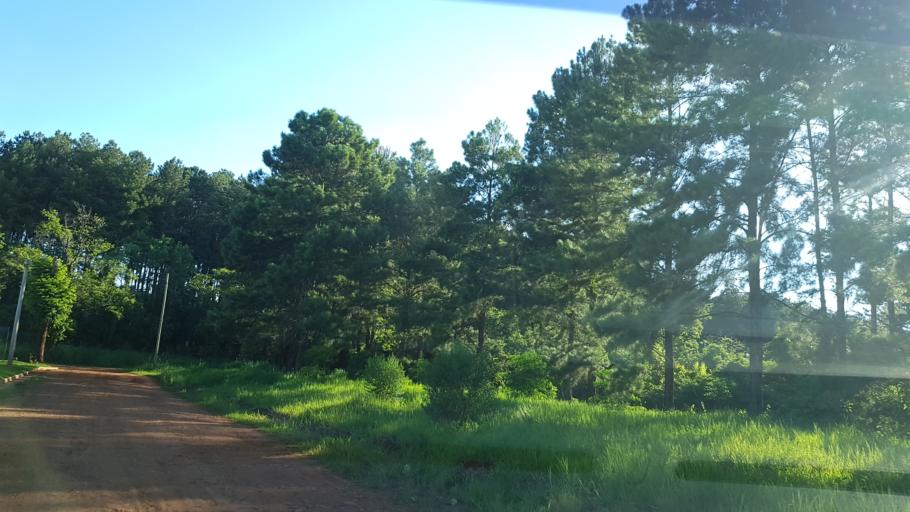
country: AR
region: Misiones
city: Puerto Libertad
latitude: -25.9199
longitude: -54.5909
